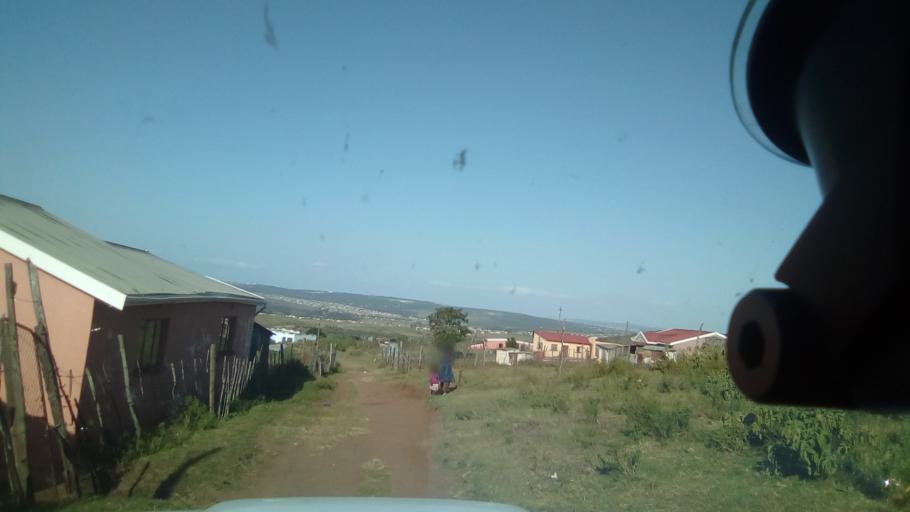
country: ZA
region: Eastern Cape
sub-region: Buffalo City Metropolitan Municipality
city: Bhisho
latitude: -32.7979
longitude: 27.3483
